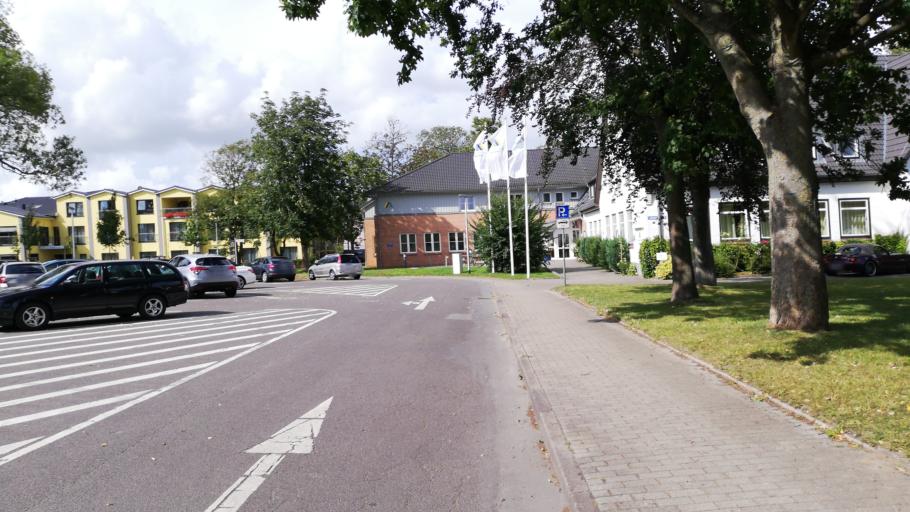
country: DE
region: Schleswig-Holstein
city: Friedrichstadt
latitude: 54.3777
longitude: 9.0923
